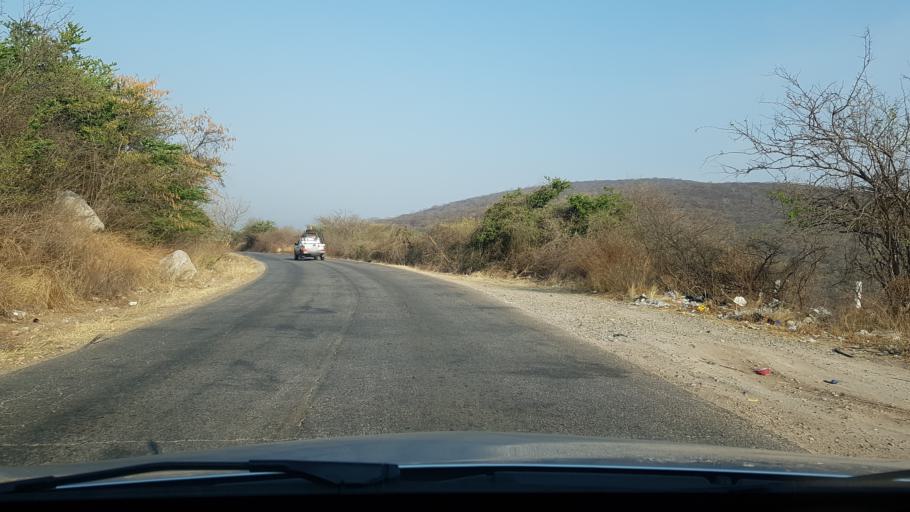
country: MX
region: Morelos
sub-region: Tlaltizapan de Zapata
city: Colonia Palo Prieto (Chipitongo)
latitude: 18.6750
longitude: -99.0617
